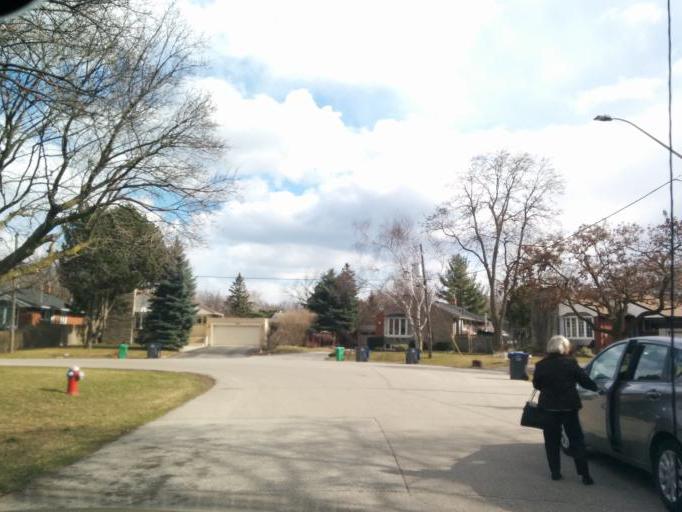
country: CA
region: Ontario
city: Etobicoke
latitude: 43.5979
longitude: -79.5662
